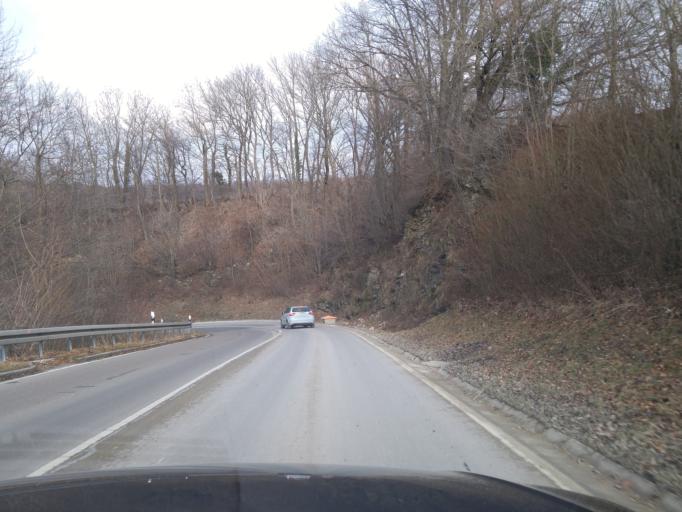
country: DE
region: Baden-Wuerttemberg
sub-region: Regierungsbezirk Stuttgart
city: Erkenbrechtsweiler
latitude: 48.5626
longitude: 9.4325
